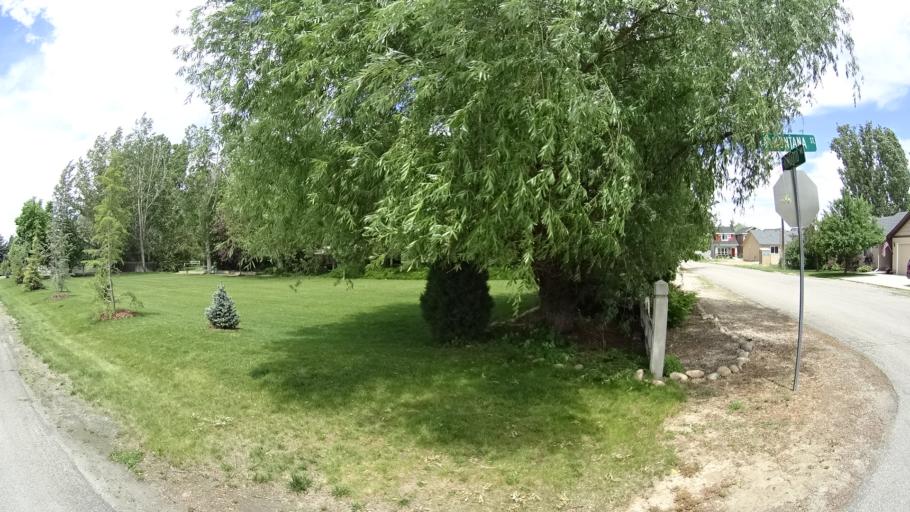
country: US
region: Idaho
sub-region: Ada County
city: Meridian
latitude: 43.6312
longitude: -116.3232
